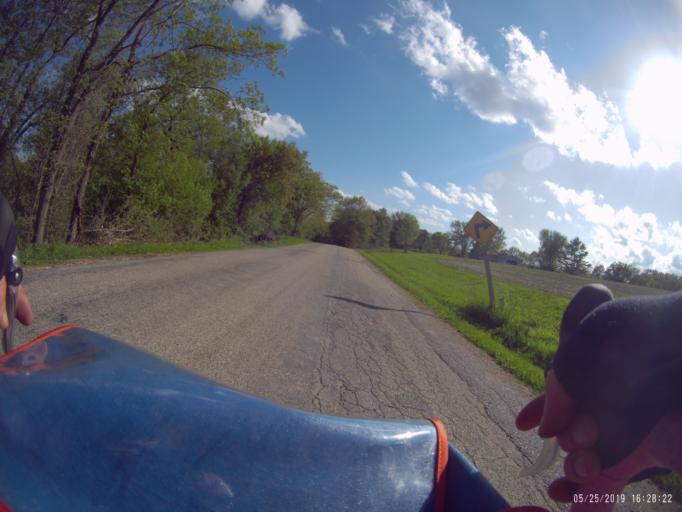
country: US
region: Wisconsin
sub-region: Dane County
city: Mount Horeb
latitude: 42.9476
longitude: -89.7070
